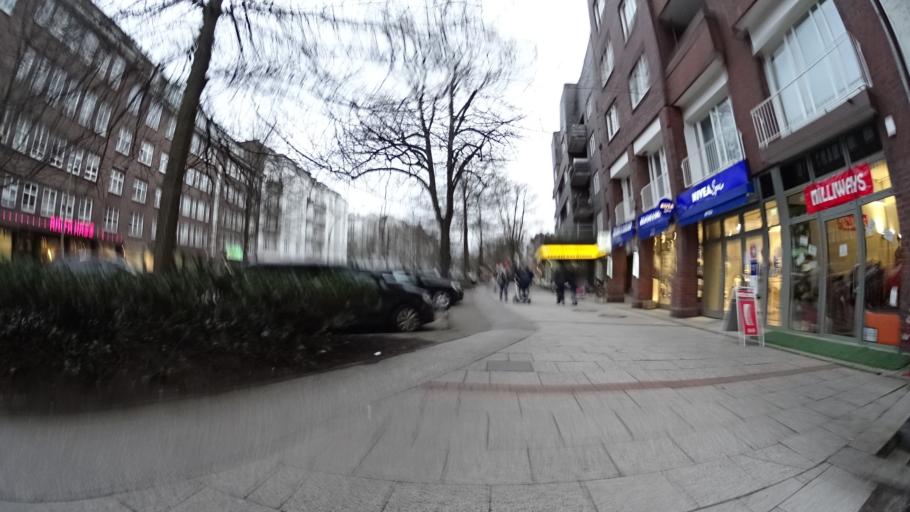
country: DE
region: Hamburg
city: Hamburg-Nord
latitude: 53.5891
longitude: 9.9864
